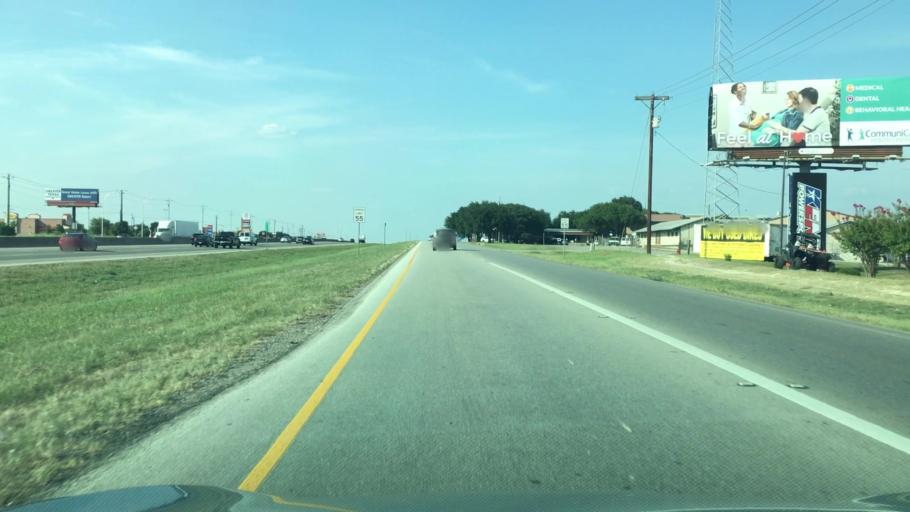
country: US
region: Texas
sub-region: Hays County
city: Kyle
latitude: 30.0062
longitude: -97.8642
